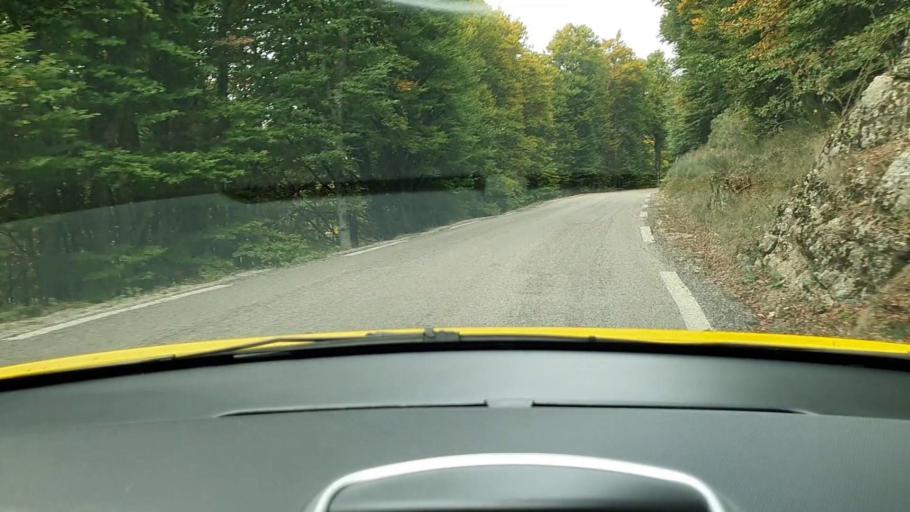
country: FR
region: Languedoc-Roussillon
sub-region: Departement du Gard
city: Le Vigan
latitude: 44.0497
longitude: 3.5540
